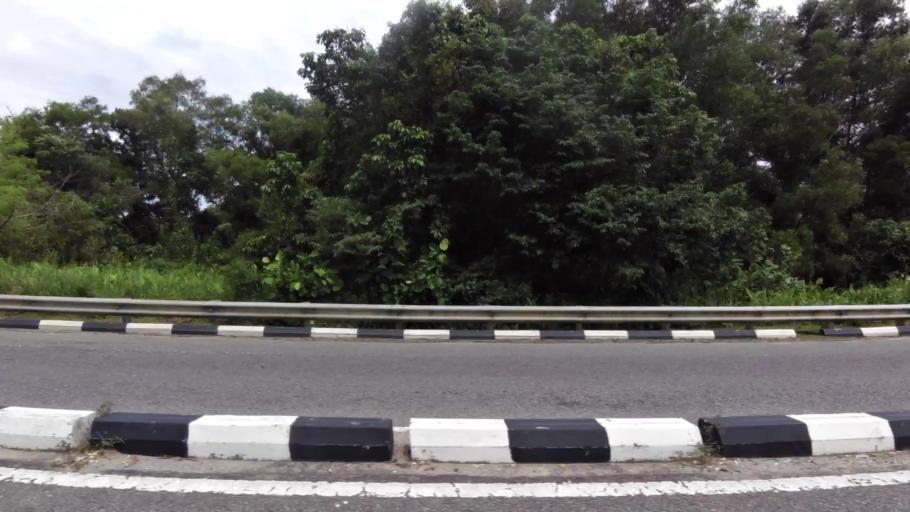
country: BN
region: Brunei and Muara
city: Bandar Seri Begawan
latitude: 4.9213
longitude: 114.9134
